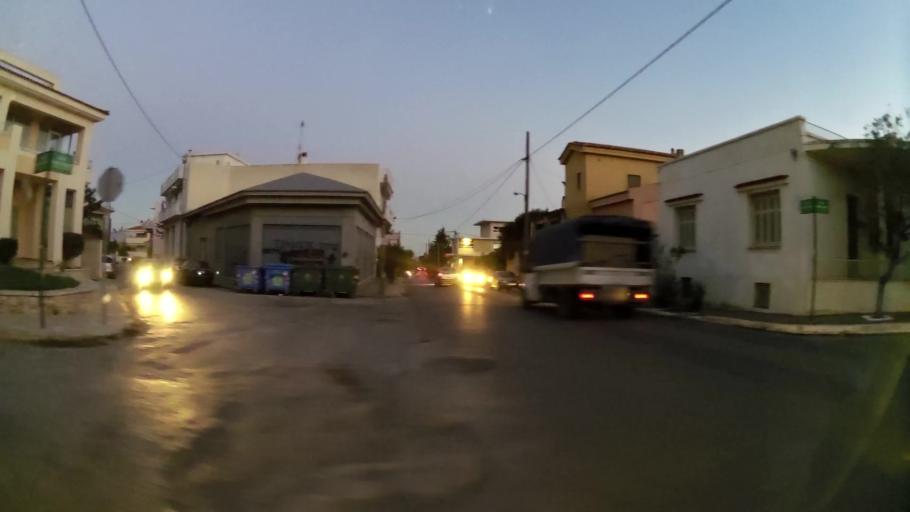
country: GR
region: Attica
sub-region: Nomarchia Anatolikis Attikis
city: Paiania
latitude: 37.9551
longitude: 23.8553
